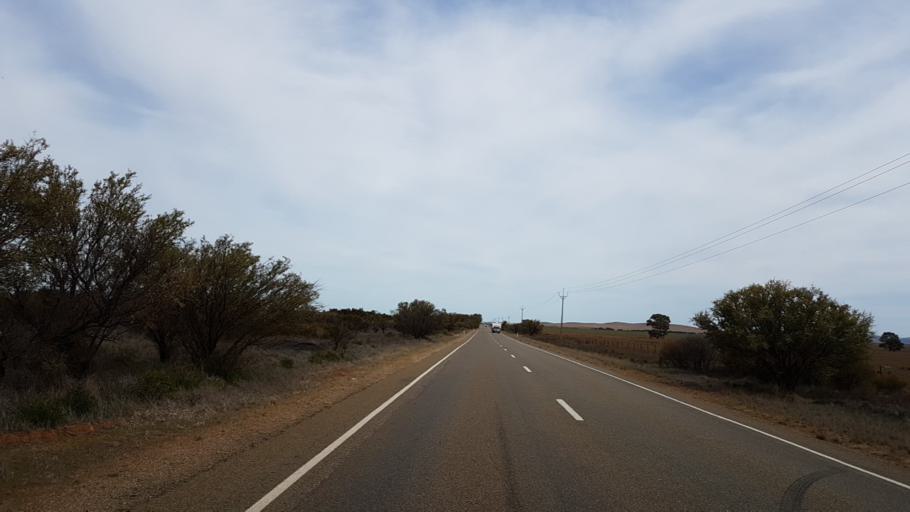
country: AU
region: South Australia
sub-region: Peterborough
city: Peterborough
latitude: -32.9946
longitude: 138.7855
